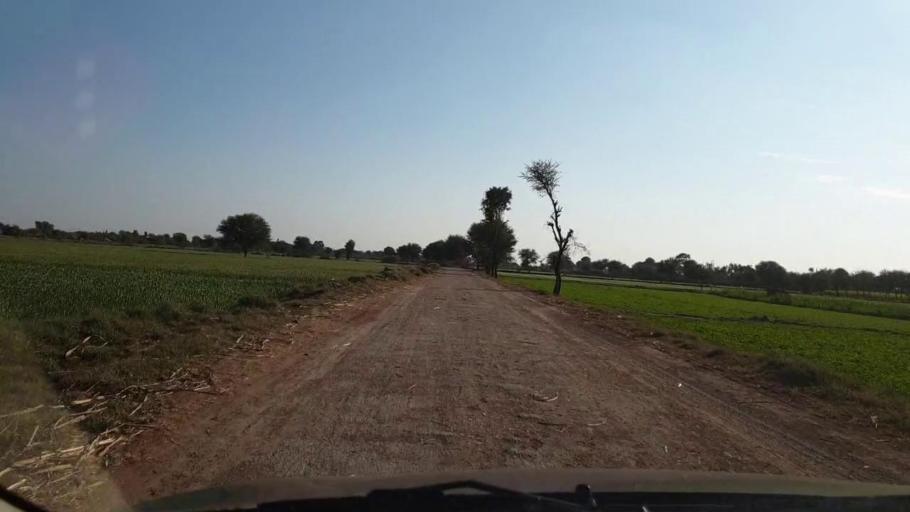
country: PK
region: Sindh
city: Jhol
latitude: 25.9644
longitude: 68.8394
